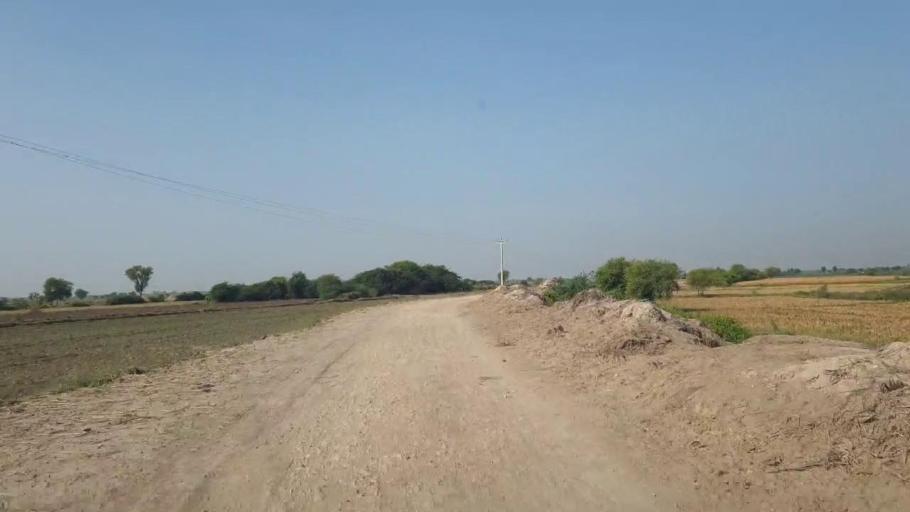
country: PK
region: Sindh
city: Badin
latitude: 24.5180
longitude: 68.7822
